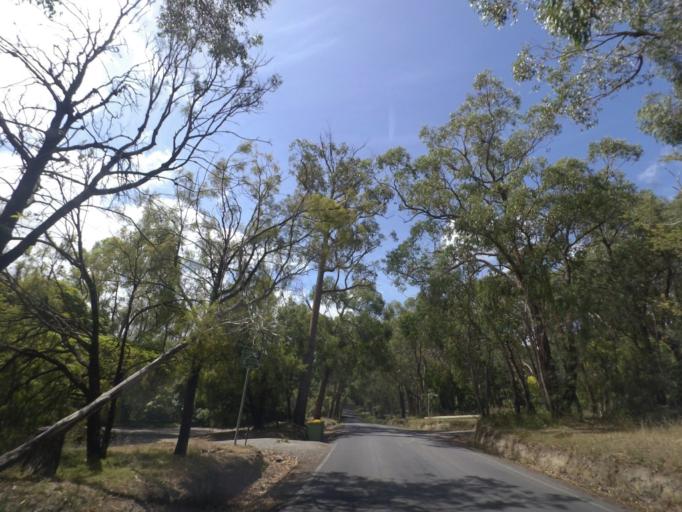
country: AU
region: Victoria
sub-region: Yarra Ranges
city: Montrose
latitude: -37.7924
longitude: 145.3536
